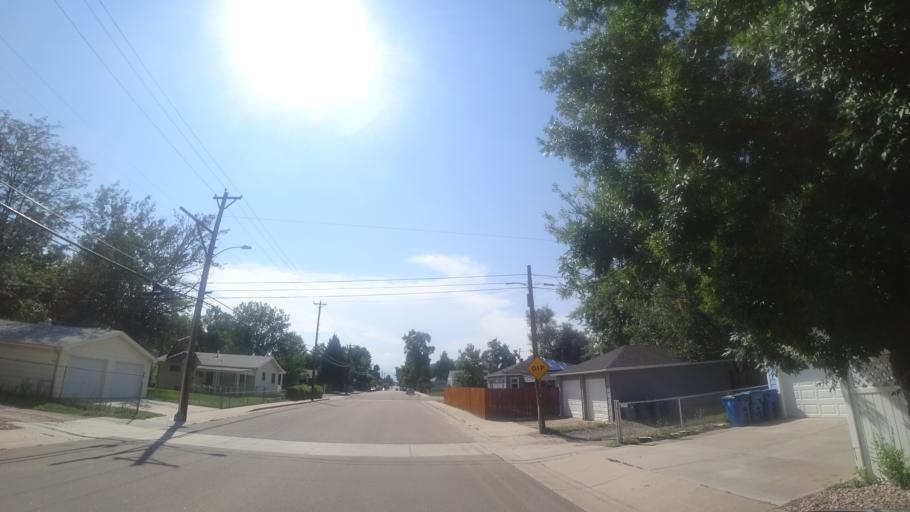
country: US
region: Colorado
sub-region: Arapahoe County
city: Englewood
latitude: 39.6386
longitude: -104.9800
